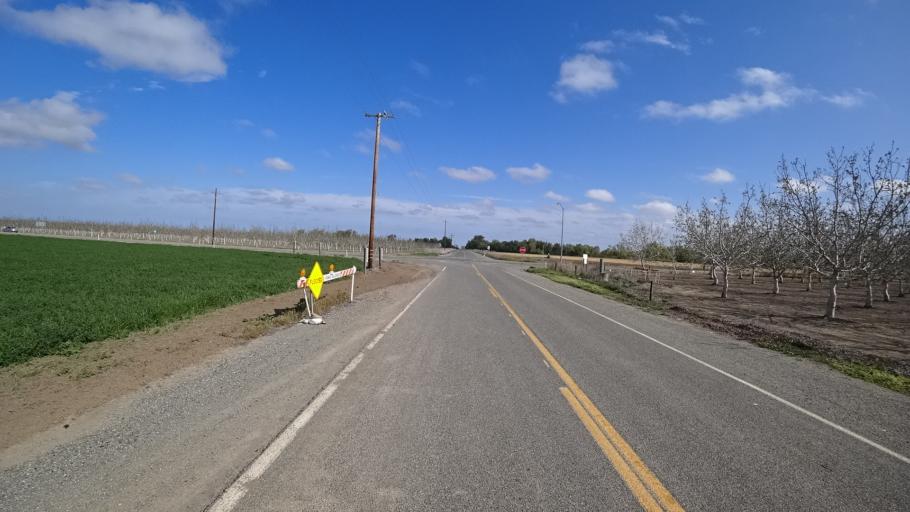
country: US
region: California
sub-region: Butte County
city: Biggs
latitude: 39.4635
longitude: -121.9302
